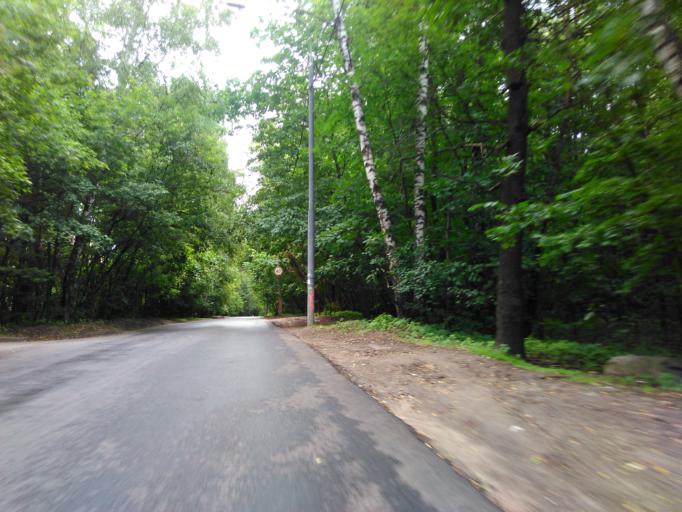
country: RU
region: Moscow
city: Rostokino
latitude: 55.8300
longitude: 37.6743
